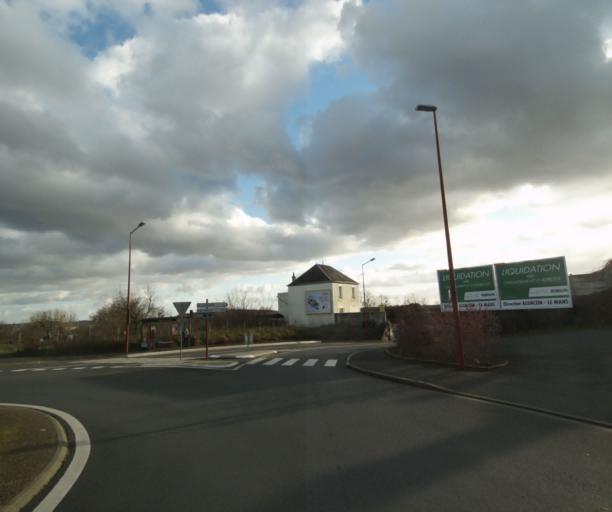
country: FR
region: Pays de la Loire
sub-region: Departement de la Sarthe
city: Allonnes
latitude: 47.9837
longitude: 0.1509
